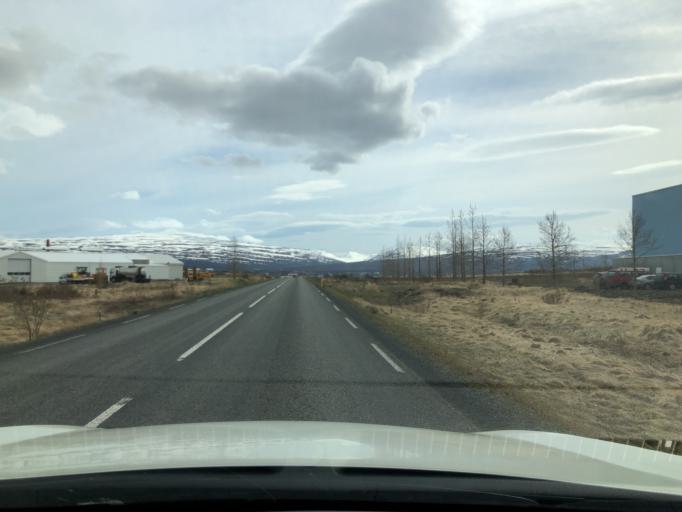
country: IS
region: East
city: Egilsstadir
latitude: 65.2972
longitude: -14.4449
